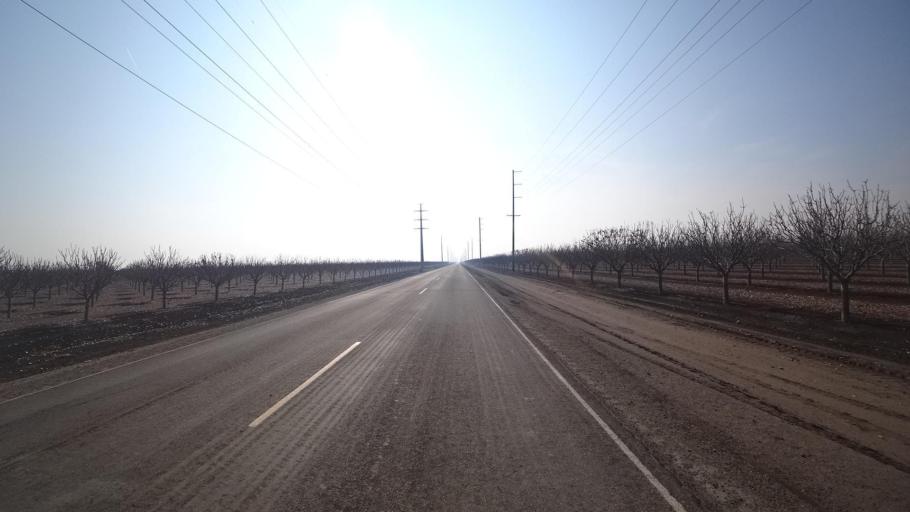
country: US
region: California
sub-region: Kern County
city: Buttonwillow
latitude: 35.3897
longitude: -119.4477
